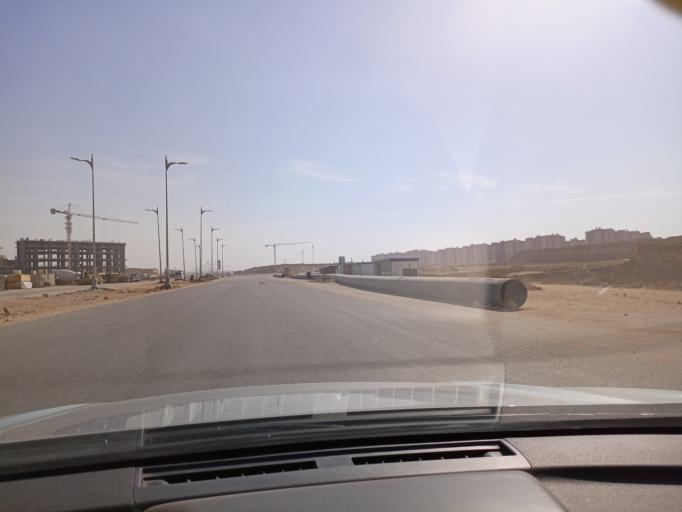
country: EG
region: Muhafazat al Qalyubiyah
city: Al Khankah
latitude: 30.0351
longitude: 31.6818
